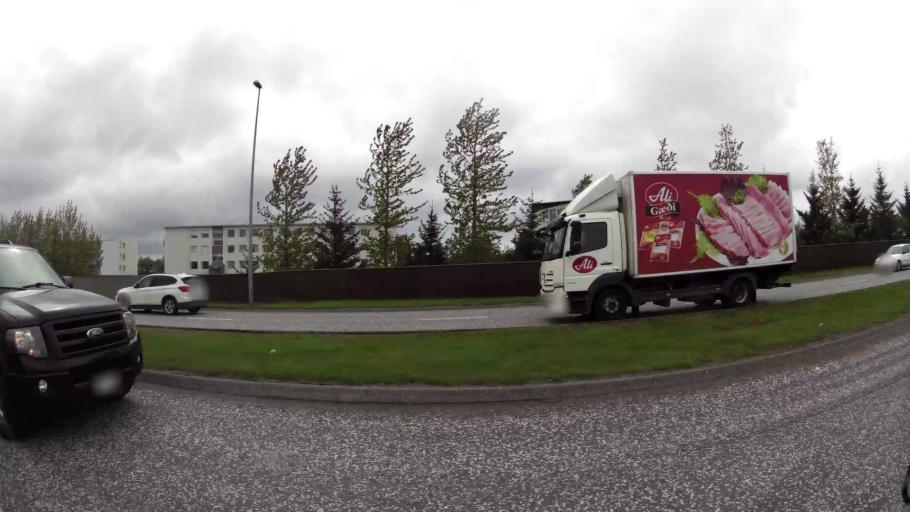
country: IS
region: Capital Region
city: Hafnarfjoerdur
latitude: 64.0751
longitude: -21.9400
